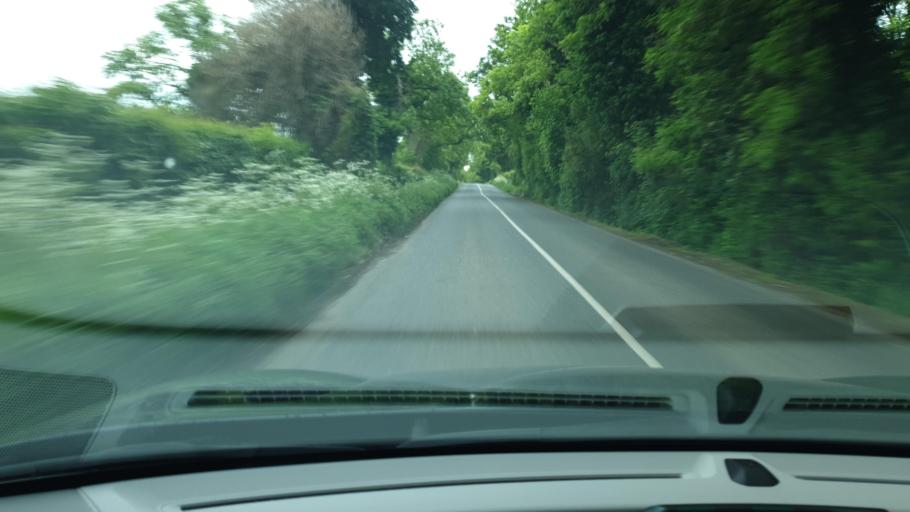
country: IE
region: Leinster
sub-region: An Mhi
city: Ashbourne
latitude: 53.5563
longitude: -6.3300
